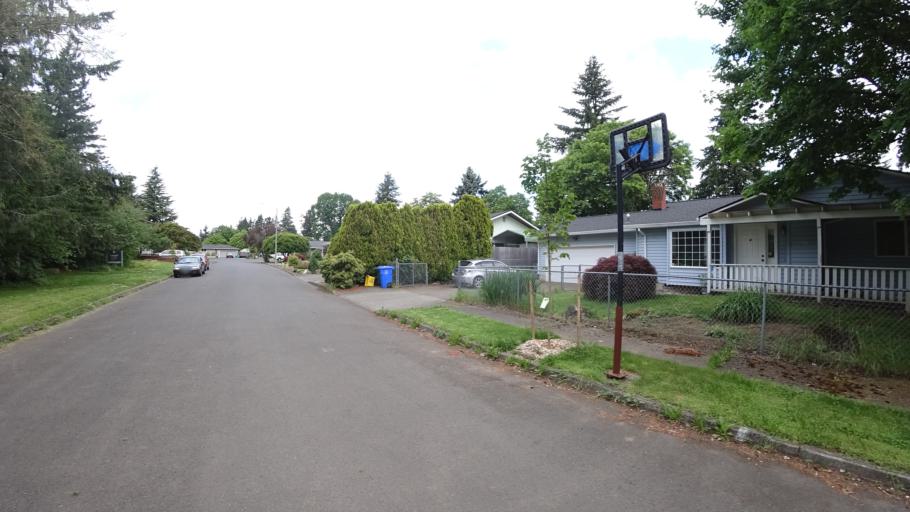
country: US
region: Oregon
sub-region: Multnomah County
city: Lents
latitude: 45.5092
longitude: -122.5493
